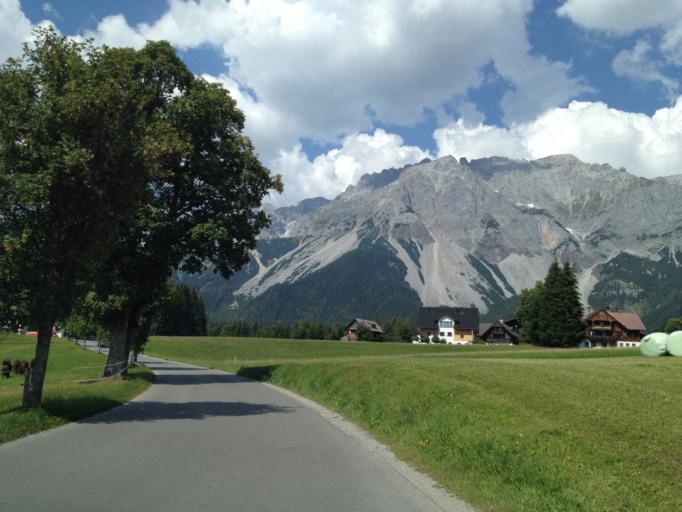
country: AT
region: Styria
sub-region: Politischer Bezirk Liezen
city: Schladming
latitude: 47.4162
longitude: 13.6382
